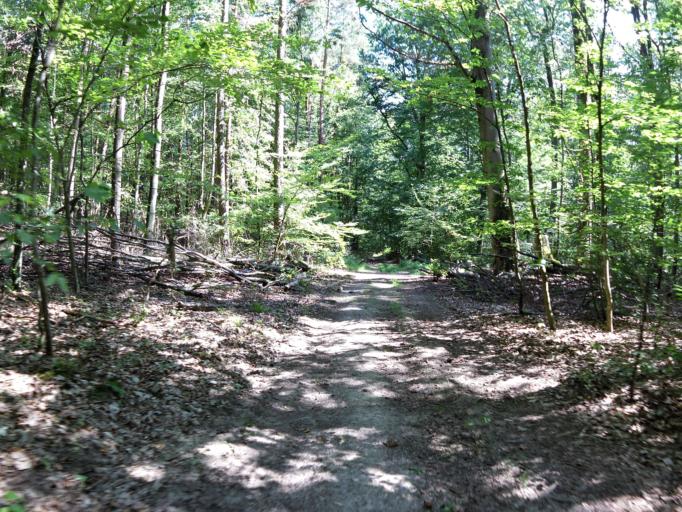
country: DE
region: Bavaria
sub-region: Regierungsbezirk Unterfranken
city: Gadheim
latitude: 49.8537
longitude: 9.8940
